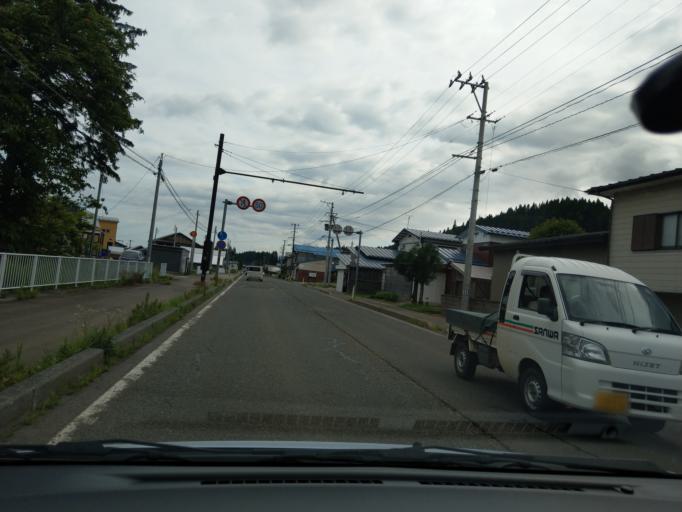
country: JP
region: Akita
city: Yokotemachi
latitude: 39.3633
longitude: 140.5656
